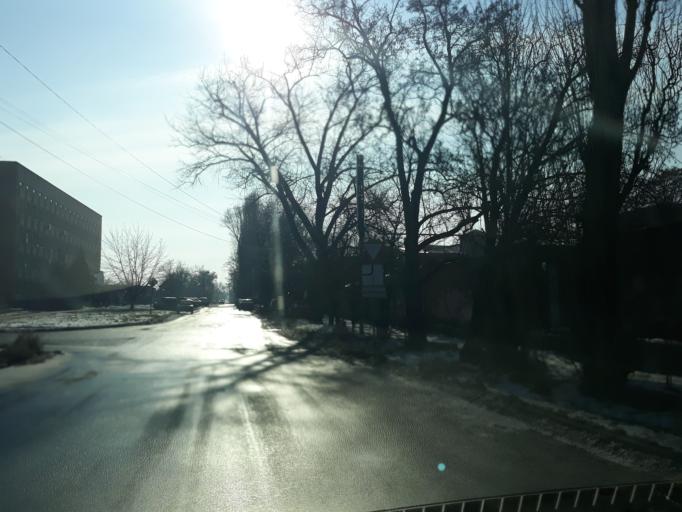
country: RU
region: Rostov
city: Taganrog
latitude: 47.2263
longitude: 38.9080
